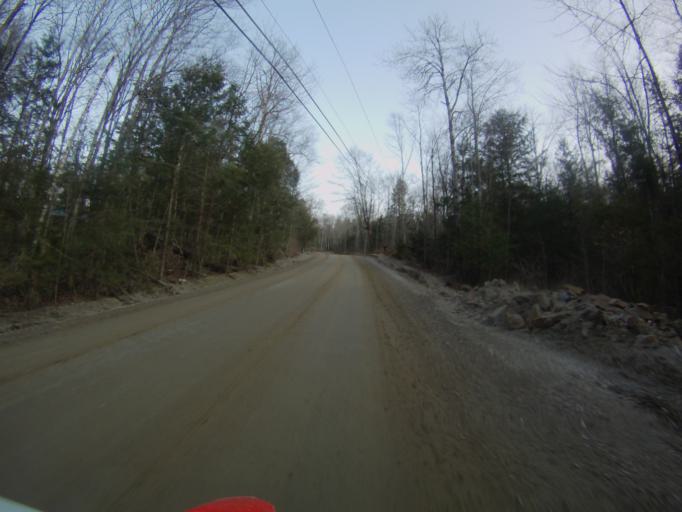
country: US
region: Vermont
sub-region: Addison County
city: Bristol
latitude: 44.0713
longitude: -73.0584
